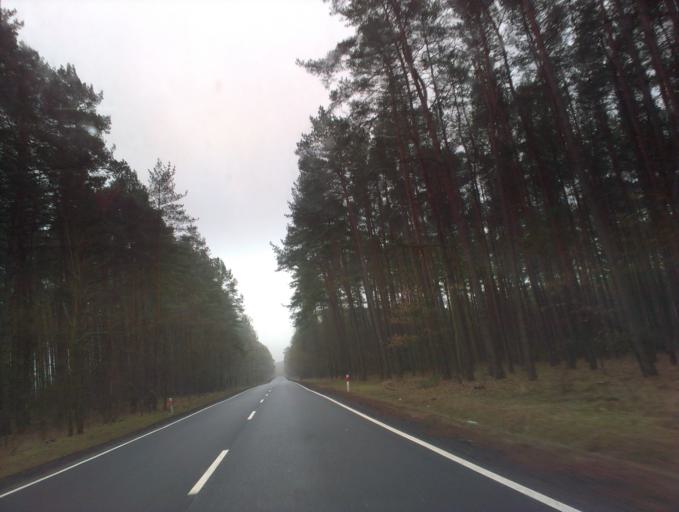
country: PL
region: Greater Poland Voivodeship
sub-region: Powiat pilski
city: Pila
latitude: 53.2460
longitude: 16.7880
